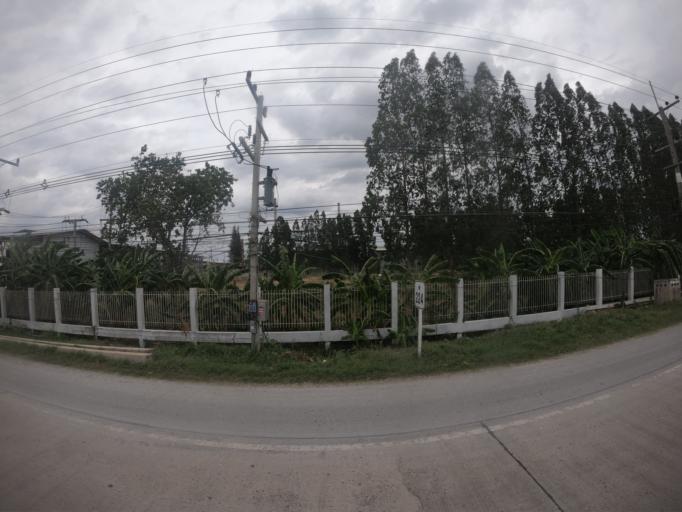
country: TH
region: Nakhon Ratchasima
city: Chok Chai
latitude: 14.8022
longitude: 102.1721
